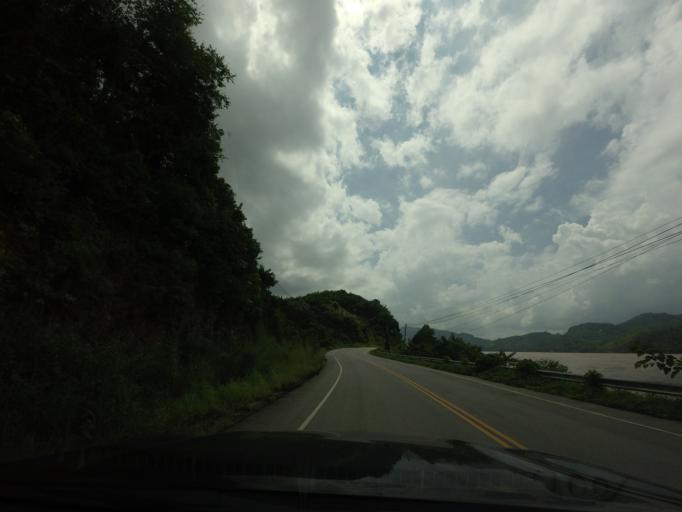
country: TH
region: Loei
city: Pak Chom
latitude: 18.0469
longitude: 101.7740
